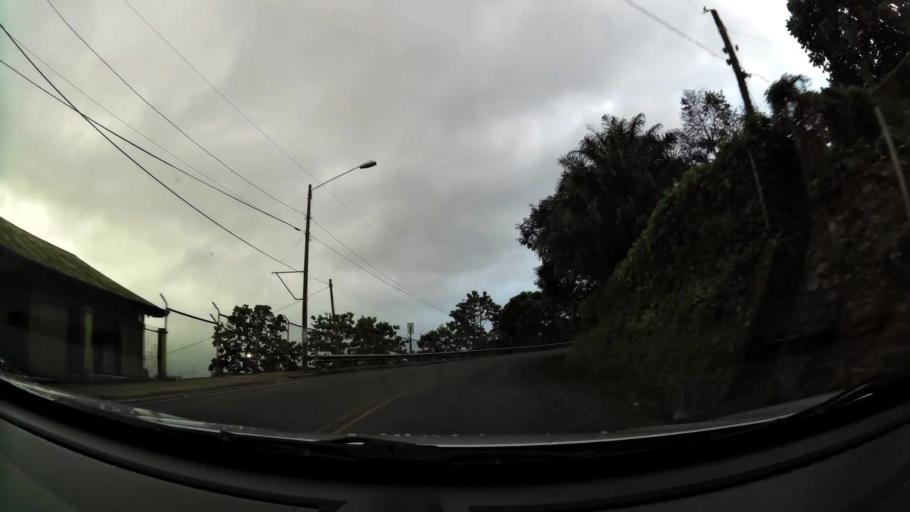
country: CR
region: Cartago
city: Turrialba
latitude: 9.9028
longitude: -83.6868
